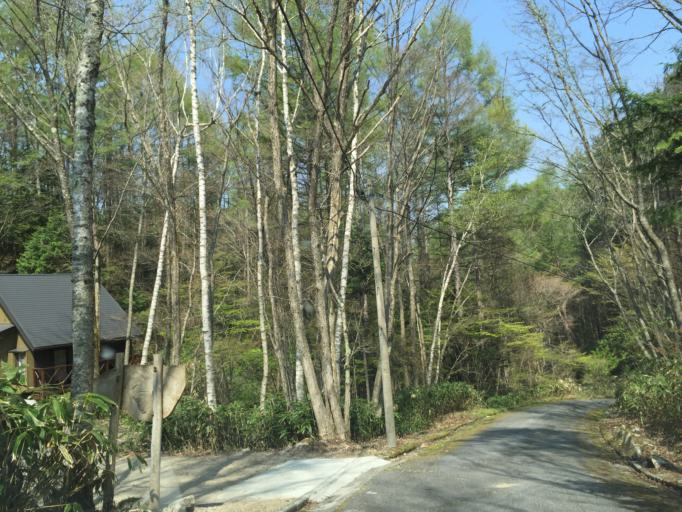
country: JP
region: Nagano
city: Iida
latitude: 35.3555
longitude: 137.6788
